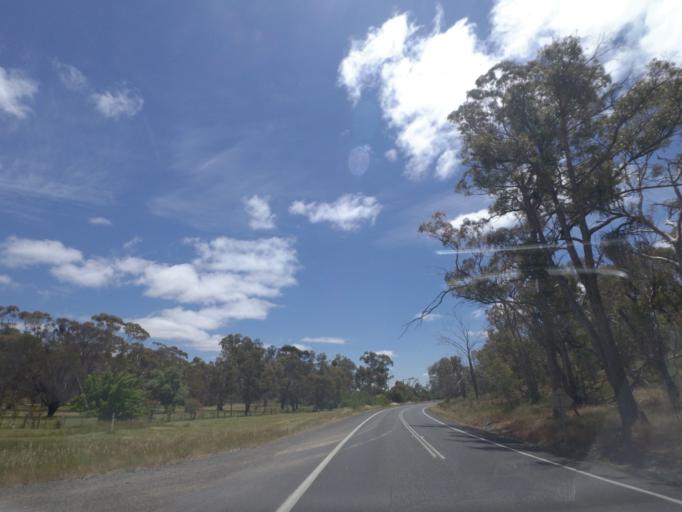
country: AU
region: Victoria
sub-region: Mount Alexander
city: Castlemaine
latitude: -37.2814
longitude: 144.1521
